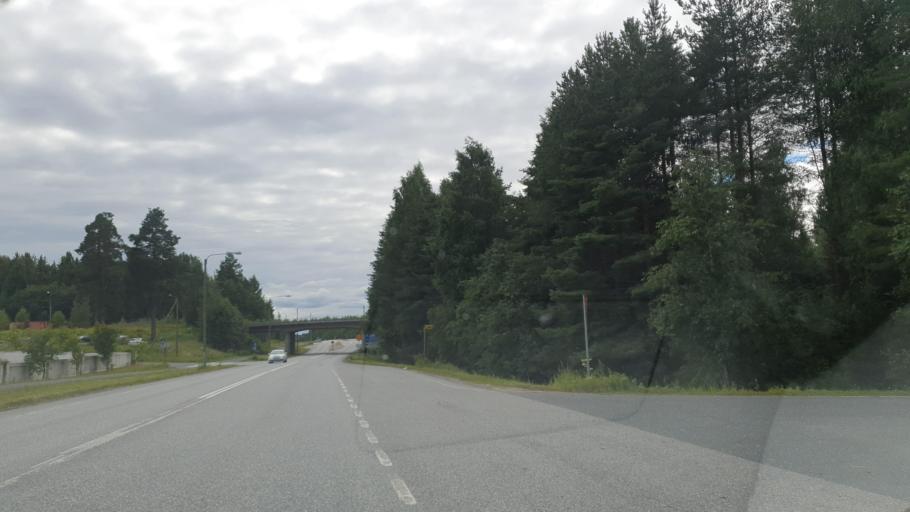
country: FI
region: Northern Savo
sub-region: Ylae-Savo
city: Iisalmi
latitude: 63.5241
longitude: 27.2464
